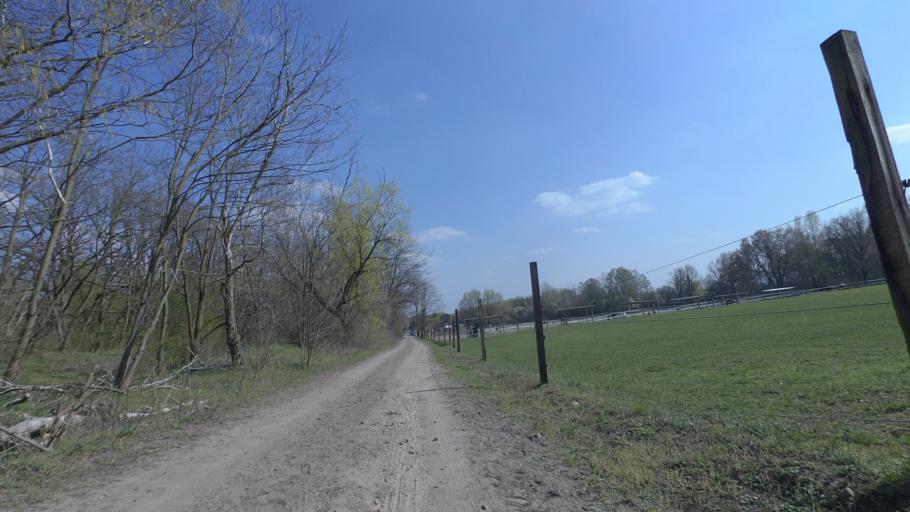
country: DE
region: Brandenburg
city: Teupitz
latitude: 52.1794
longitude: 13.5599
